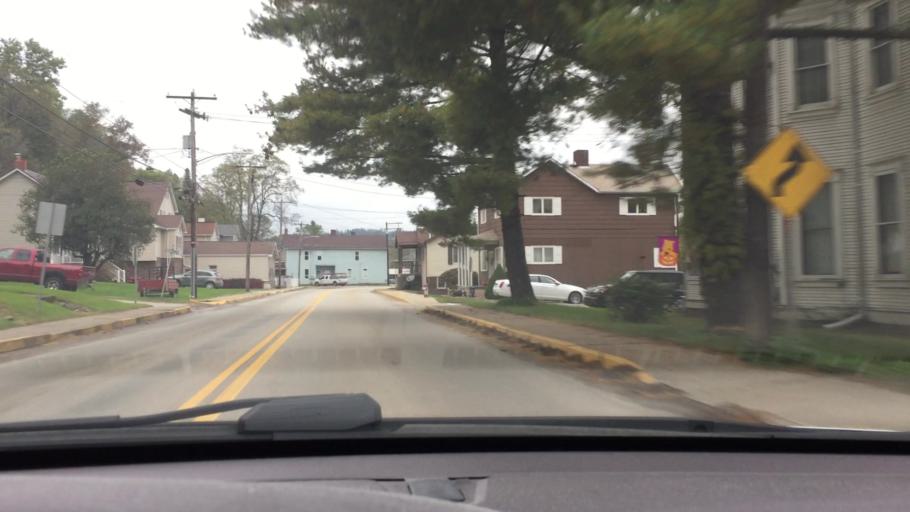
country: US
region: Pennsylvania
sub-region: Fayette County
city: Fairhope
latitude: 40.0978
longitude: -79.8447
